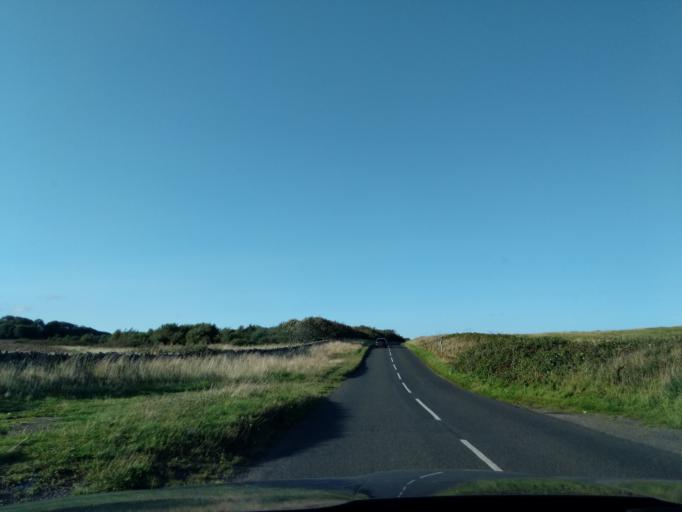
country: GB
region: England
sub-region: Northumberland
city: Lynemouth
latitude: 55.2199
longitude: -1.5303
